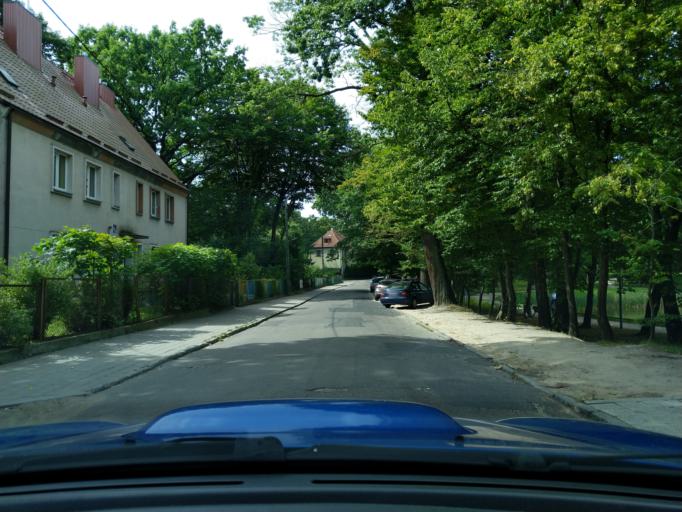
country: PL
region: Warmian-Masurian Voivodeship
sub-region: Powiat olsztynski
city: Olsztyn
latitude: 53.7920
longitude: 20.4818
